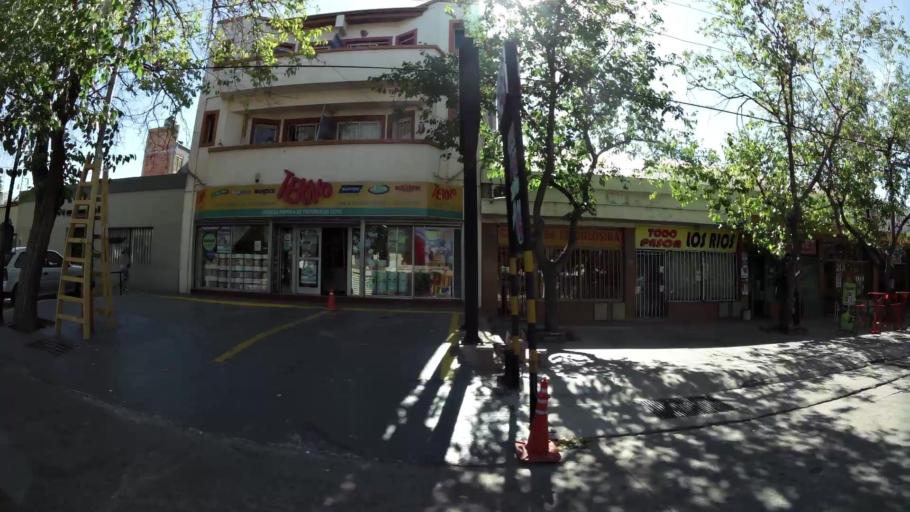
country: AR
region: Mendoza
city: Villa Nueva
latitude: -32.9041
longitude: -68.7891
